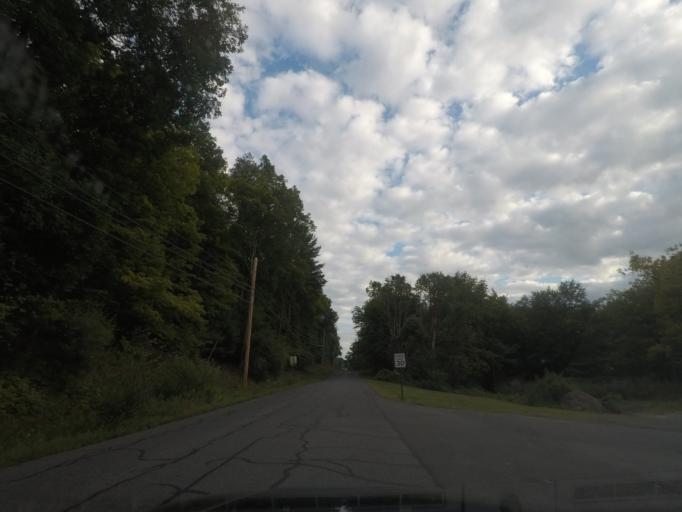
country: US
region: New York
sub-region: Rensselaer County
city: Nassau
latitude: 42.5118
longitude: -73.6089
